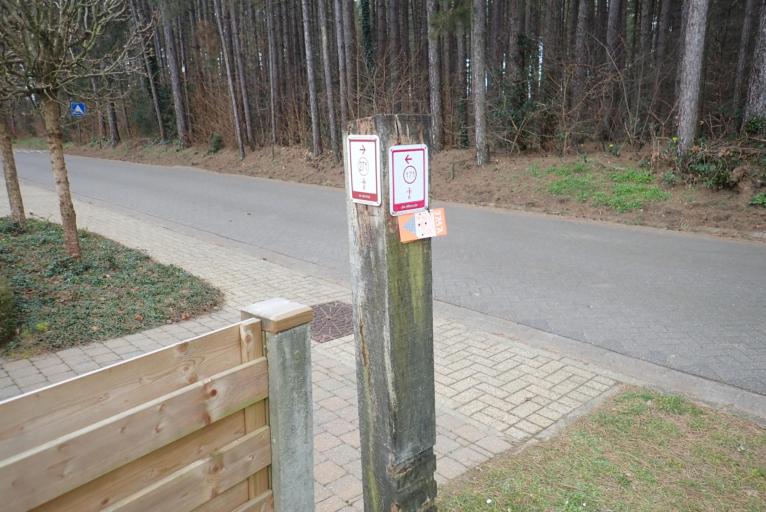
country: BE
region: Flanders
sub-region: Provincie Antwerpen
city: Herselt
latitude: 51.0408
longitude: 4.9318
